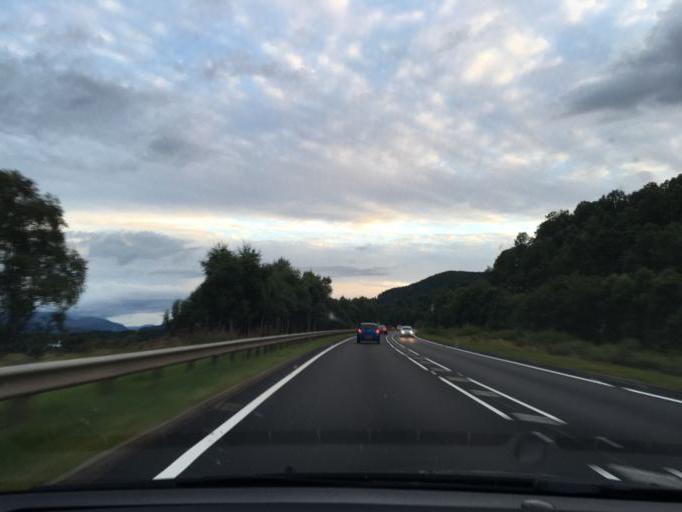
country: GB
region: Scotland
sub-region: Highland
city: Aviemore
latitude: 57.2328
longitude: -3.8117
